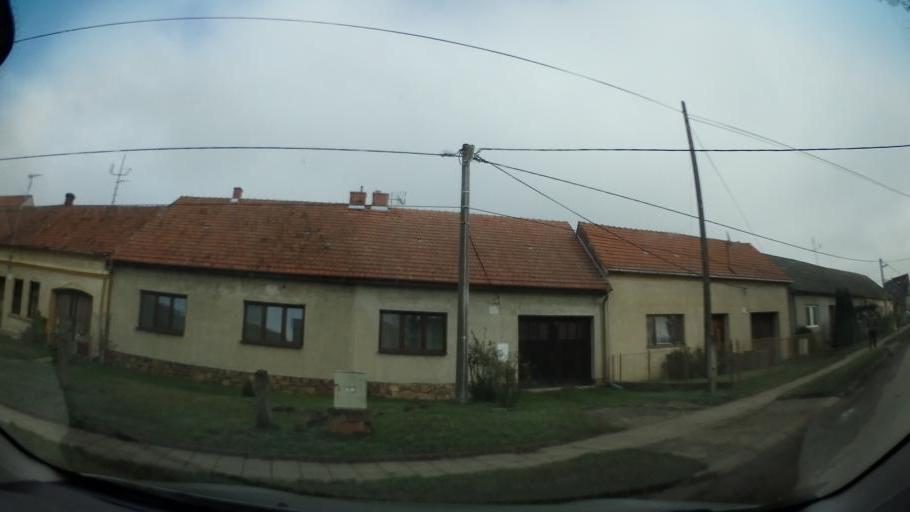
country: CZ
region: Vysocina
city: Mohelno
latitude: 49.1232
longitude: 16.2484
